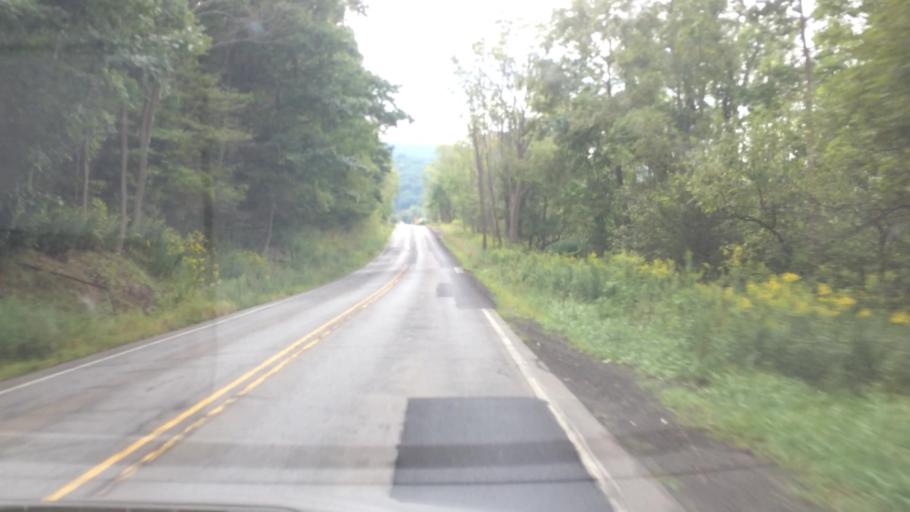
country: US
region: Pennsylvania
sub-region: McKean County
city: Bradford
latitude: 41.9184
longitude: -78.6438
